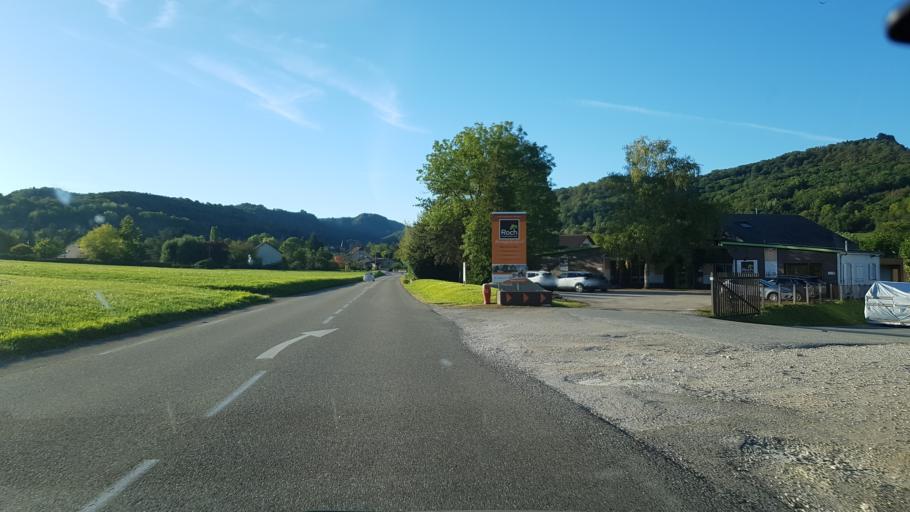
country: FR
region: Franche-Comte
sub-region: Departement du Jura
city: Lons-le-Saunier
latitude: 46.6520
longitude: 5.5380
